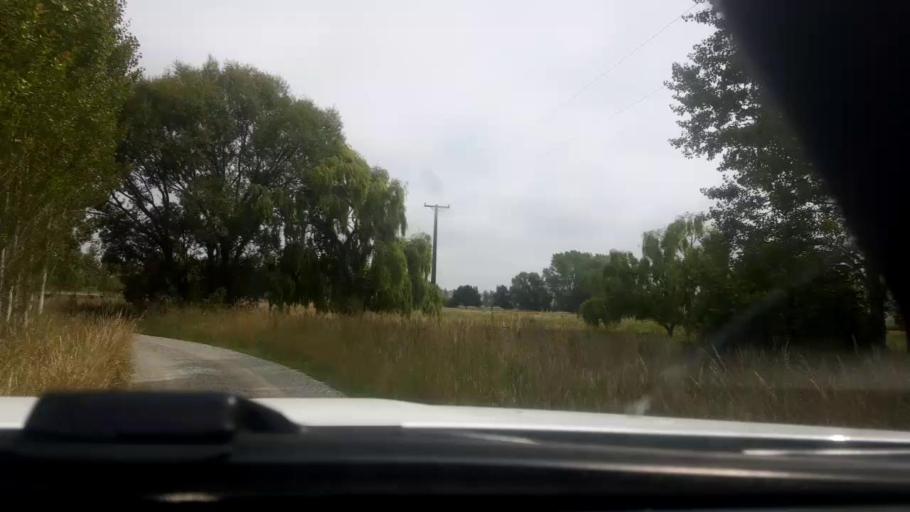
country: NZ
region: Canterbury
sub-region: Timaru District
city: Pleasant Point
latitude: -44.3256
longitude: 171.1951
